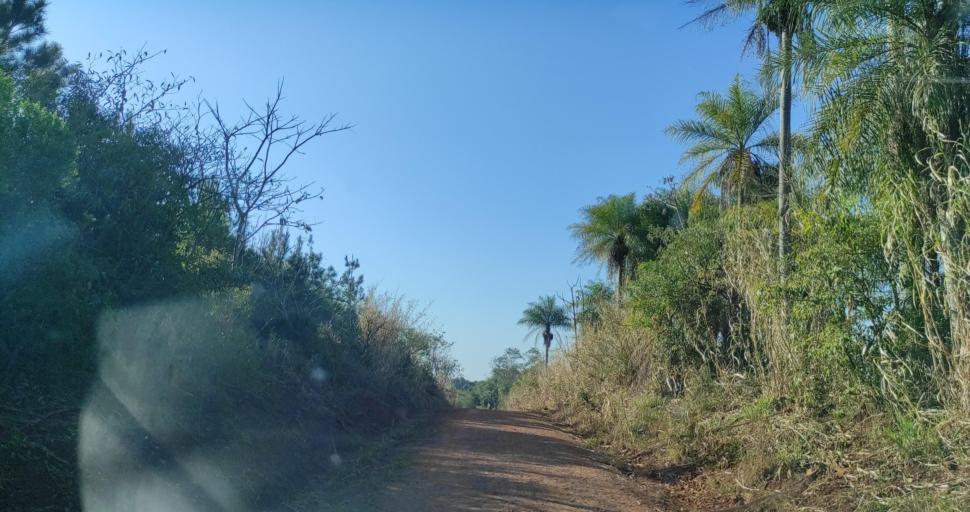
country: AR
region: Misiones
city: Capiovi
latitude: -26.8819
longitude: -55.1076
